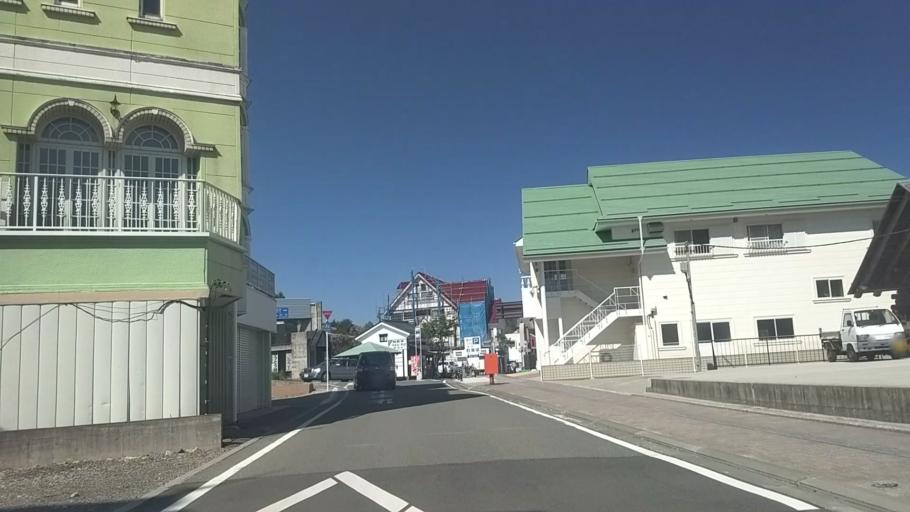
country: JP
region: Yamanashi
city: Nirasaki
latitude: 35.9180
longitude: 138.4356
